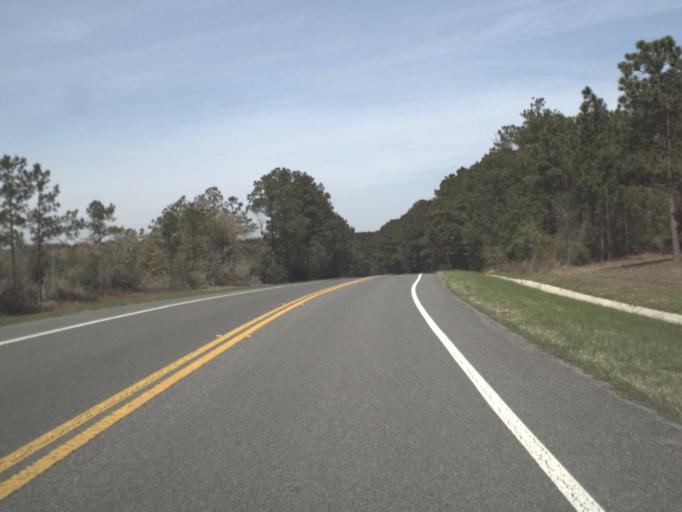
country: US
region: Florida
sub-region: Walton County
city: DeFuniak Springs
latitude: 30.7172
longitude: -86.0193
